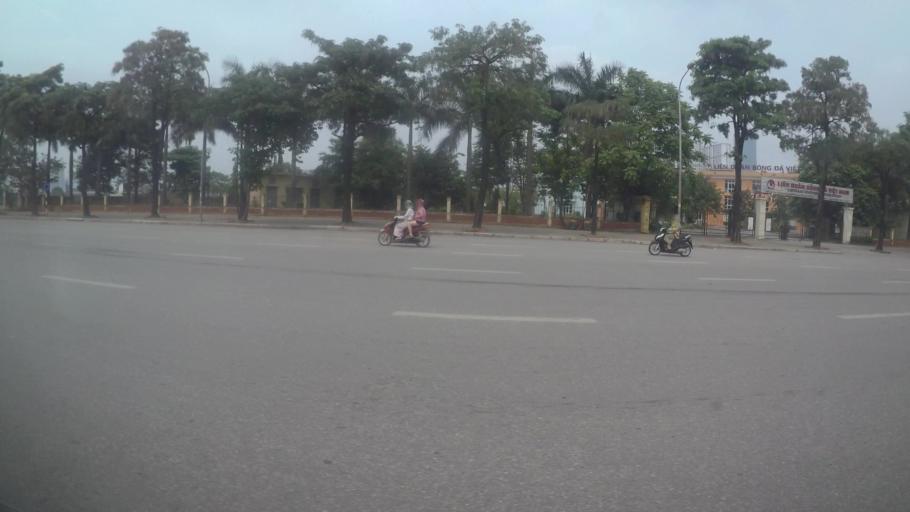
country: VN
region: Ha Noi
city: Cau Dien
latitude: 21.0164
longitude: 105.7680
